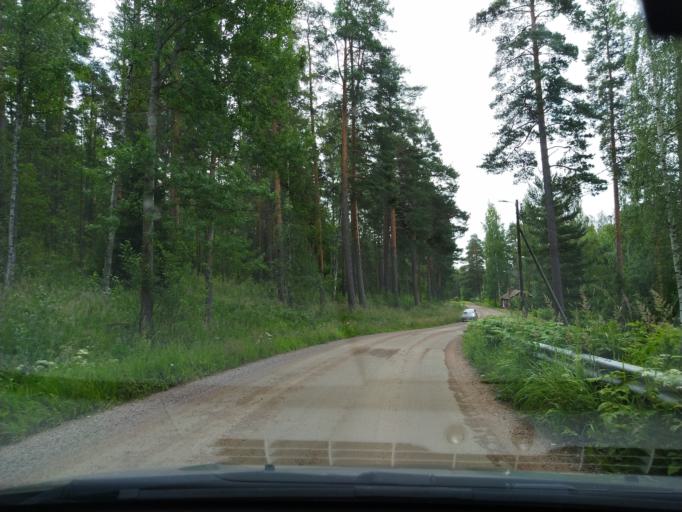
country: FI
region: Kymenlaakso
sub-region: Kouvola
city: Jaala
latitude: 61.0607
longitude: 26.6463
